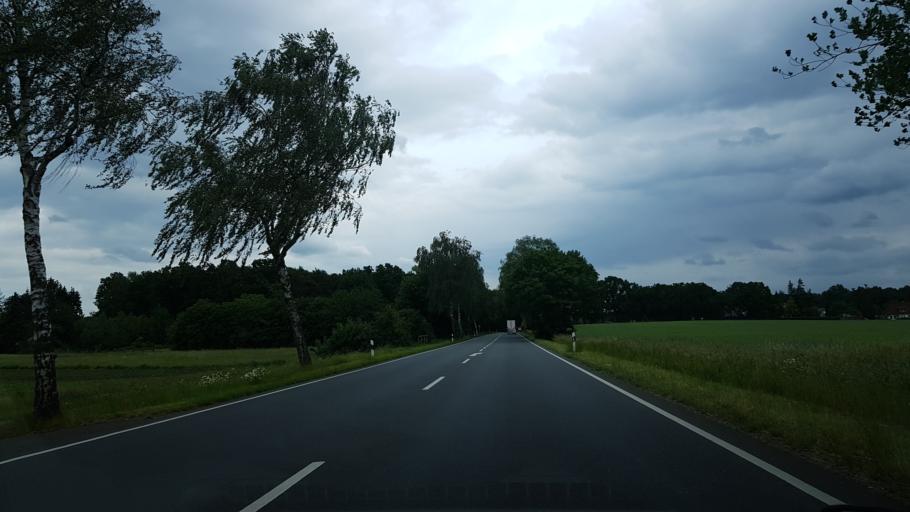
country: DE
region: Lower Saxony
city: Bergen
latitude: 52.7762
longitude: 9.9780
